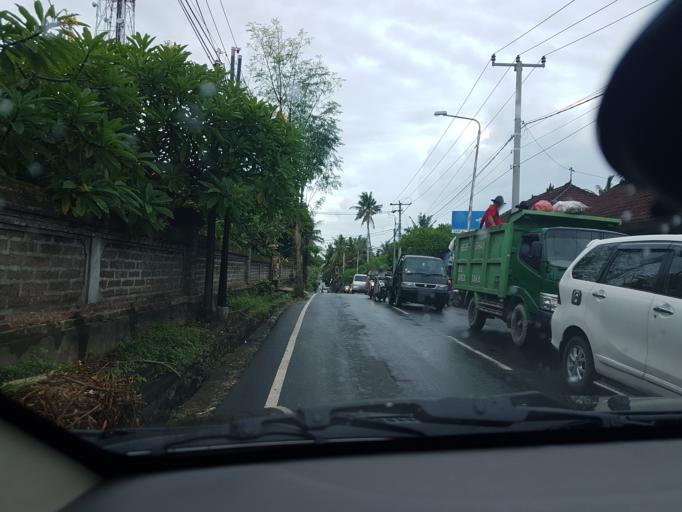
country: ID
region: Bali
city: Banjar Desa
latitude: -8.5799
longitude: 115.2387
